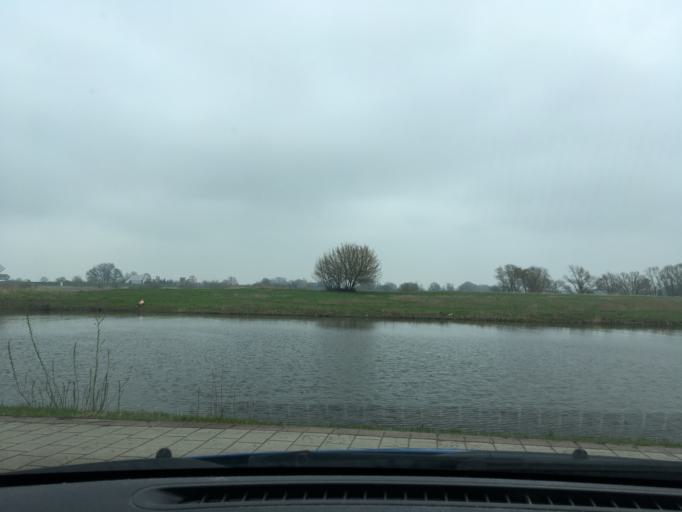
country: DE
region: Lower Saxony
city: Bleckede
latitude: 53.2980
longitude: 10.7347
